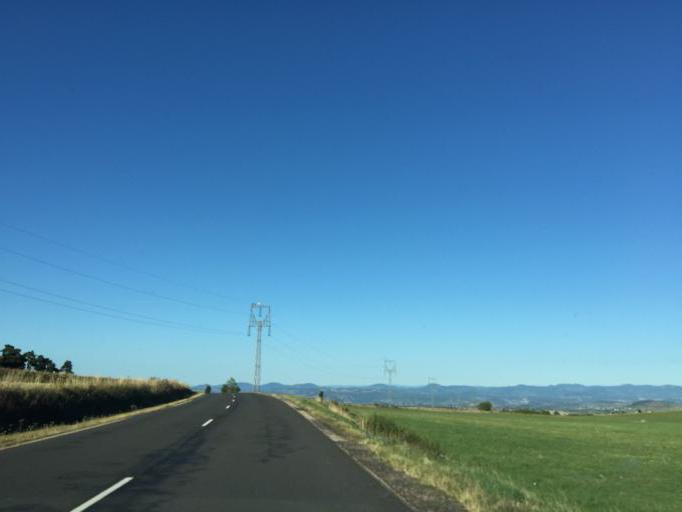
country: FR
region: Auvergne
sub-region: Departement de la Haute-Loire
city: Bains
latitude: 44.9947
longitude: 3.7479
